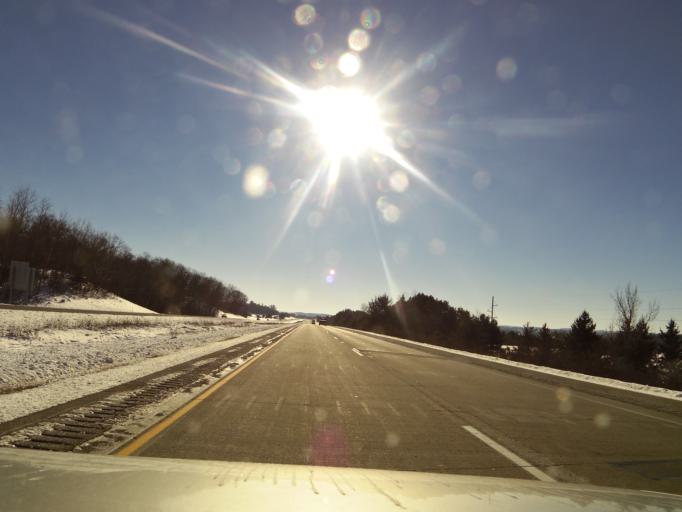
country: US
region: Wisconsin
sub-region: Monroe County
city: Tomah
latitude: 44.1098
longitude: -90.5338
